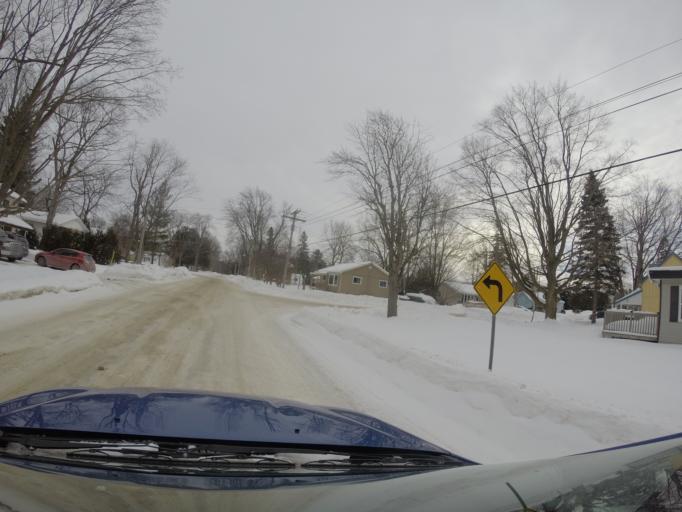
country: CA
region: Ontario
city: Wasaga Beach
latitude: 44.4190
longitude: -80.0811
